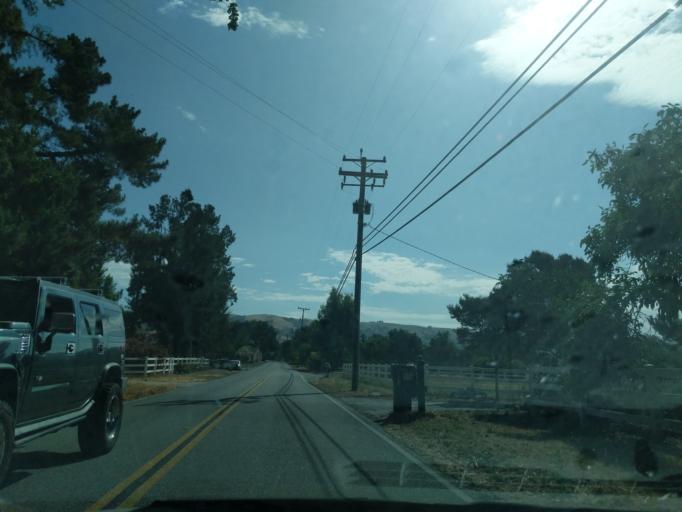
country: US
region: California
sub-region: Santa Clara County
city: Gilroy
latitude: 37.0430
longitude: -121.5387
